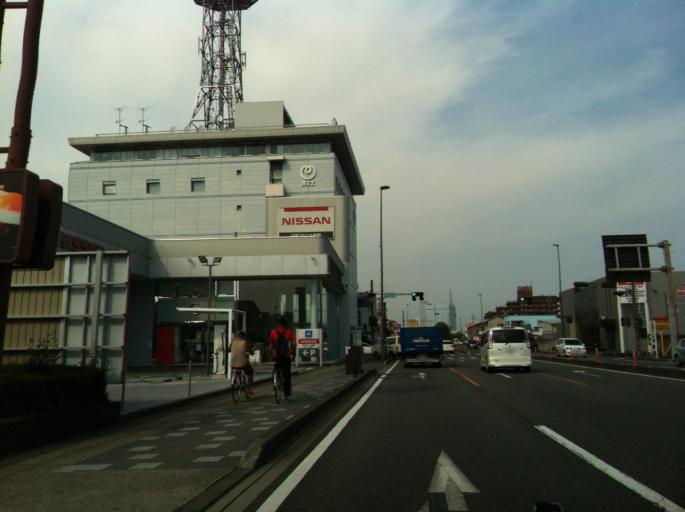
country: JP
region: Shizuoka
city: Shizuoka-shi
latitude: 35.0119
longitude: 138.4511
